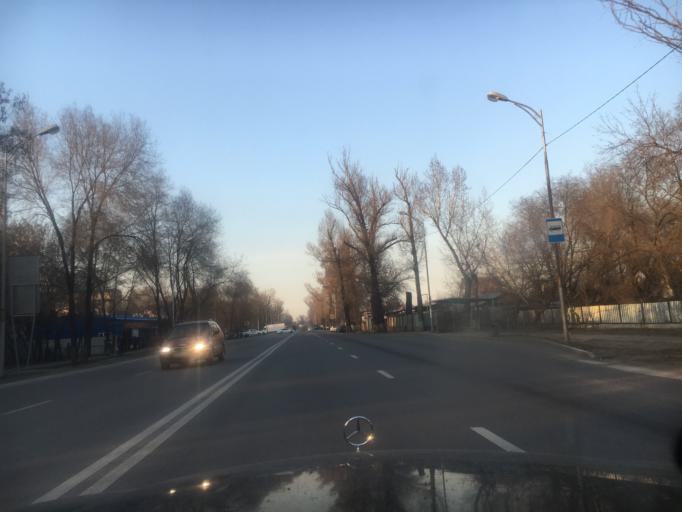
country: KZ
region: Almaty Oblysy
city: Pervomayskiy
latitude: 43.3744
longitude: 76.9915
